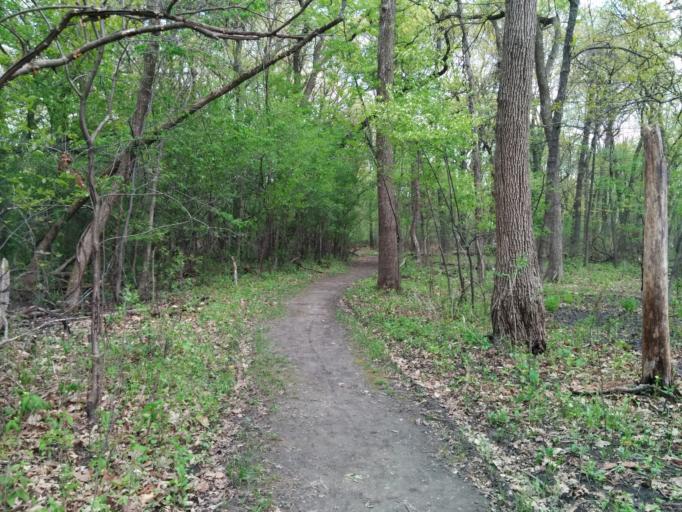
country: US
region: Illinois
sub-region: Cook County
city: River Forest
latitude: 41.8973
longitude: -87.8285
